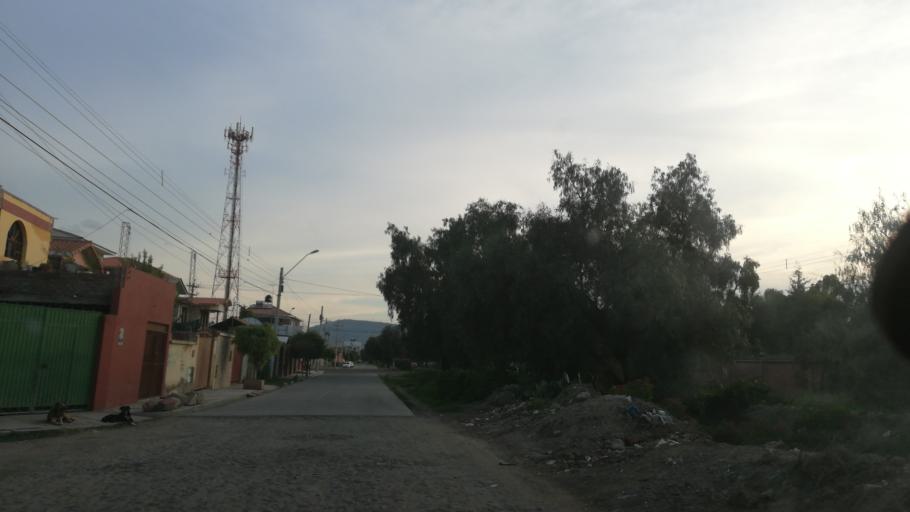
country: BO
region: Cochabamba
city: Cochabamba
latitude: -17.3807
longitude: -66.1961
